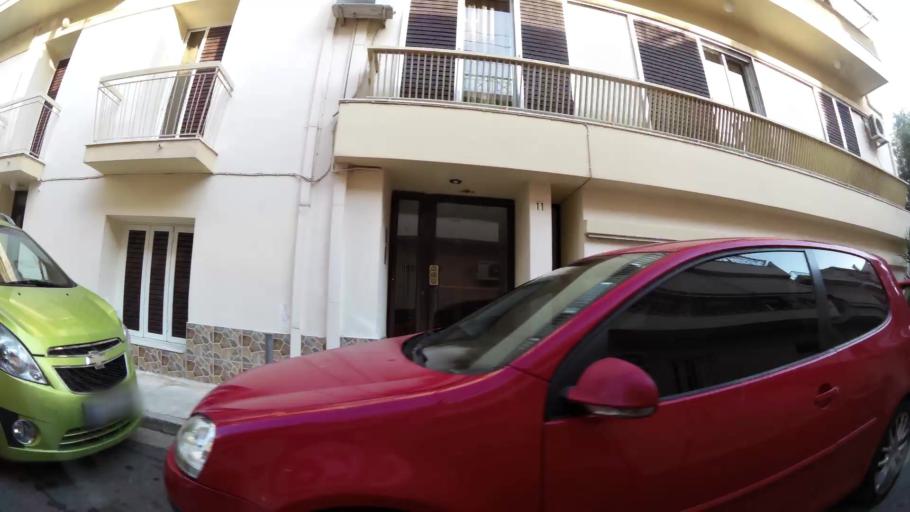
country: GR
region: Attica
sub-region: Nomarchia Athinas
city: Dhafni
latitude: 37.9515
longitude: 23.7271
